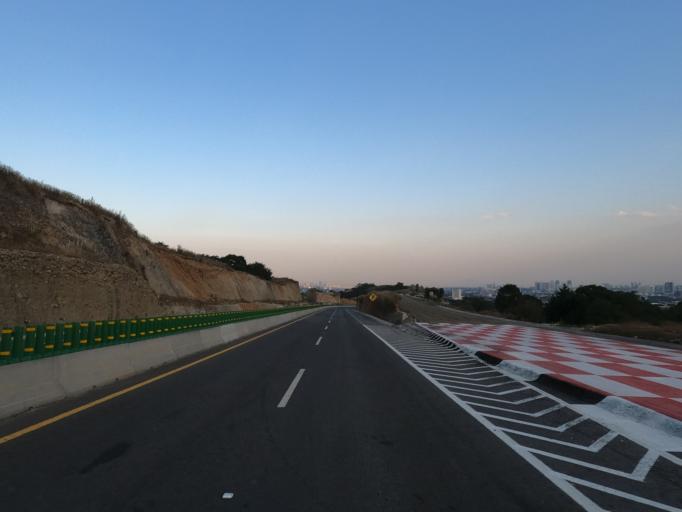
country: MX
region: Mexico
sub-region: Naucalpan de Juarez
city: Llano de las Flores (Barrio del Hueso)
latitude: 19.4224
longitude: -99.3232
